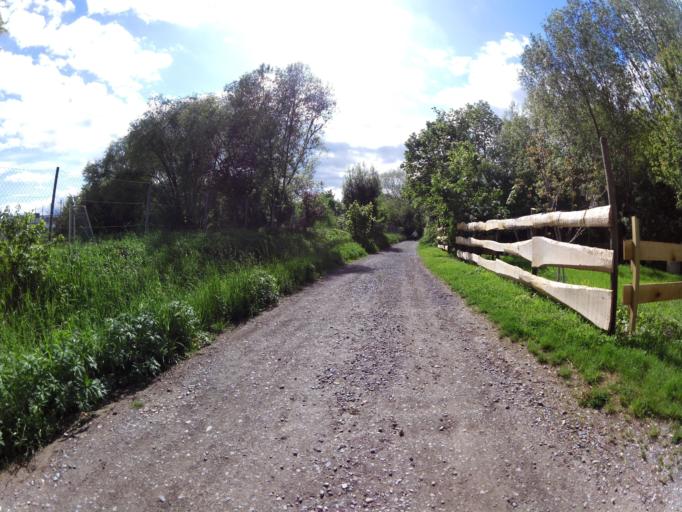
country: DE
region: Bavaria
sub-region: Regierungsbezirk Unterfranken
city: Volkach
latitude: 49.8675
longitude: 10.2334
